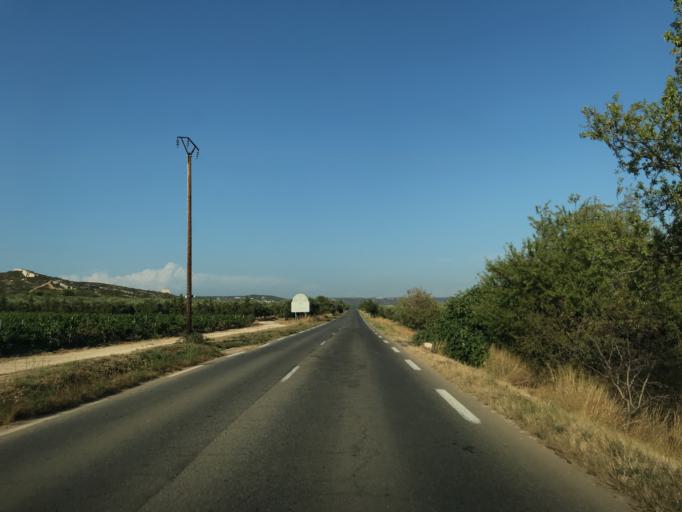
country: FR
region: Provence-Alpes-Cote d'Azur
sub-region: Departement des Bouches-du-Rhone
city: Lancon-Provence
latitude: 43.5390
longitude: 5.1236
